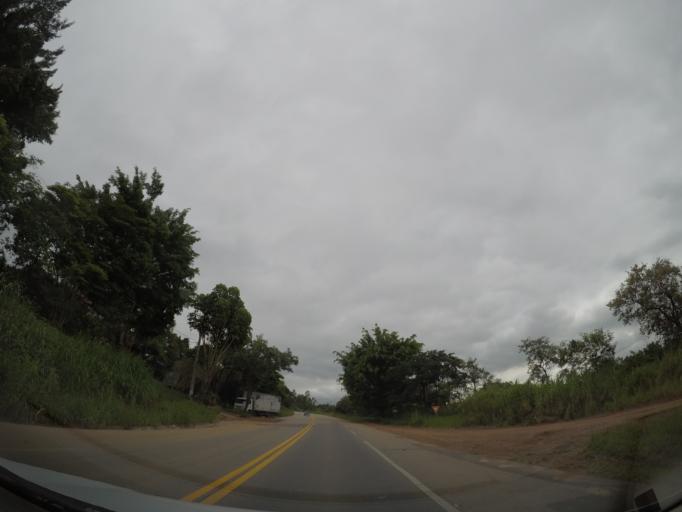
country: BR
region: Sao Paulo
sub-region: Louveira
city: Louveira
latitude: -23.1164
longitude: -46.9402
